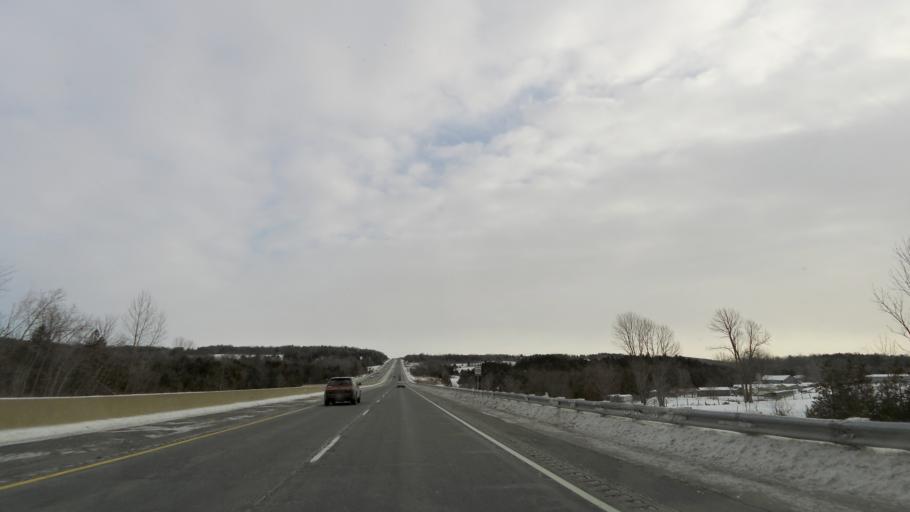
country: CA
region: Ontario
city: Cobourg
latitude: 44.0155
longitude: -77.9564
